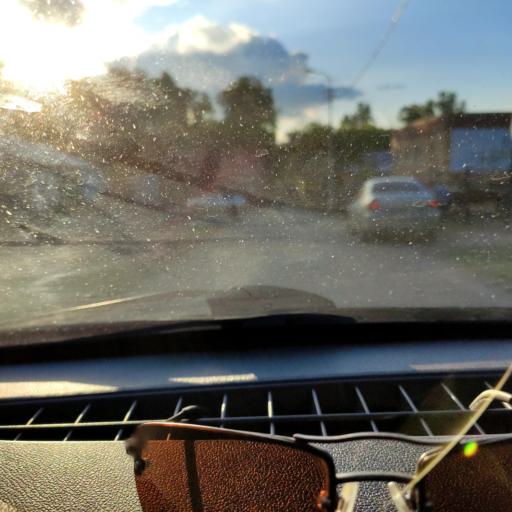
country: RU
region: Bashkortostan
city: Ufa
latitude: 54.7757
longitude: 56.0183
